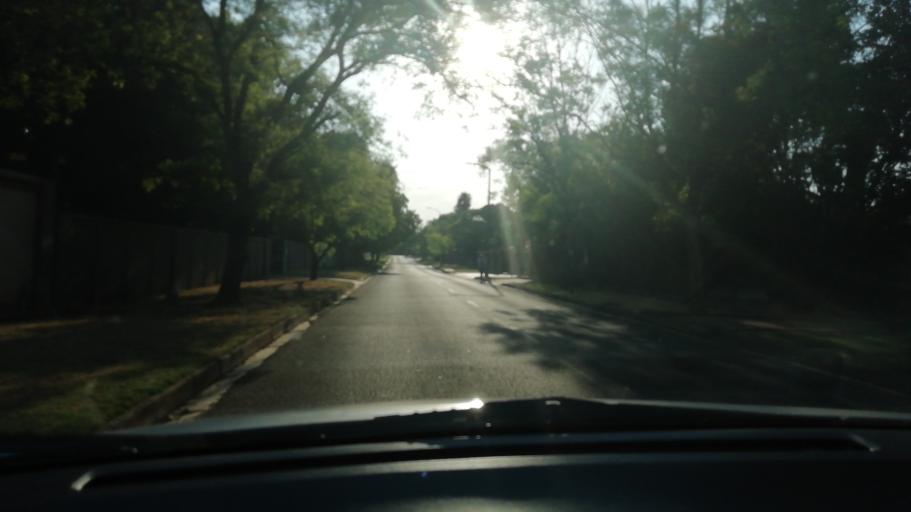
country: ZA
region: Gauteng
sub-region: Ekurhuleni Metropolitan Municipality
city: Benoni
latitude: -26.1807
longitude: 28.2860
